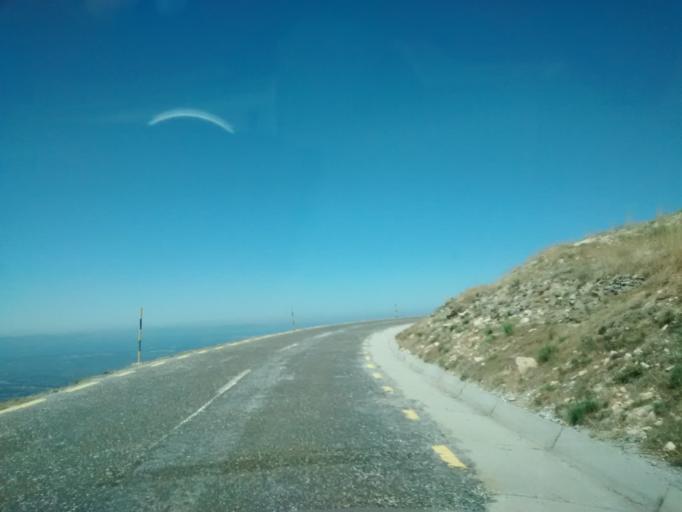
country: PT
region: Guarda
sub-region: Seia
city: Seia
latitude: 40.4190
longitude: -7.6365
